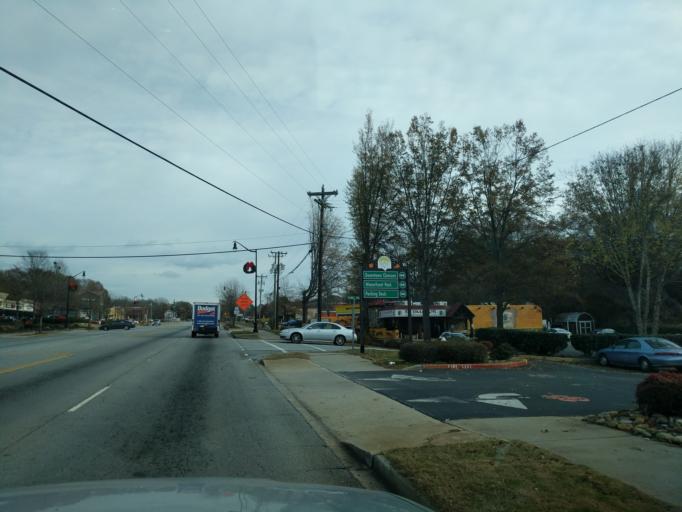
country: US
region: South Carolina
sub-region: Pickens County
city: Clemson
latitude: 34.6917
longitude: -82.8400
